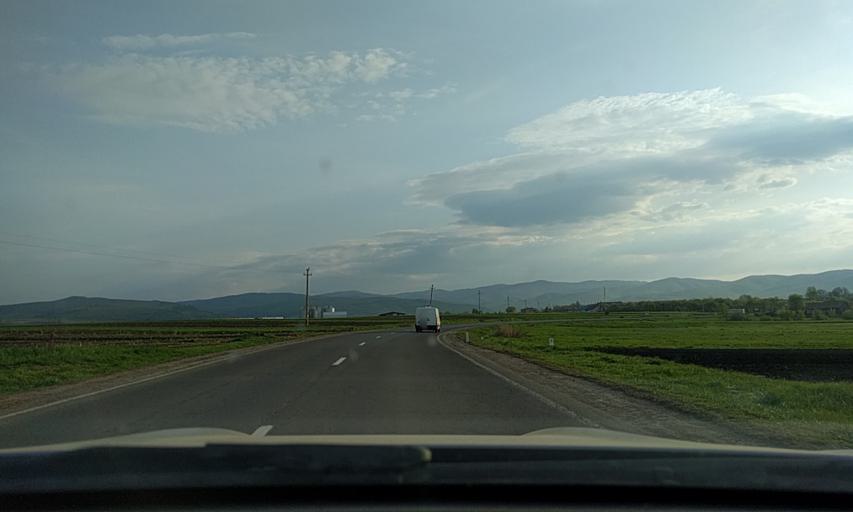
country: RO
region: Covasna
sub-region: Comuna Lemnia
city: Lemnia
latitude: 46.0436
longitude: 26.2518
